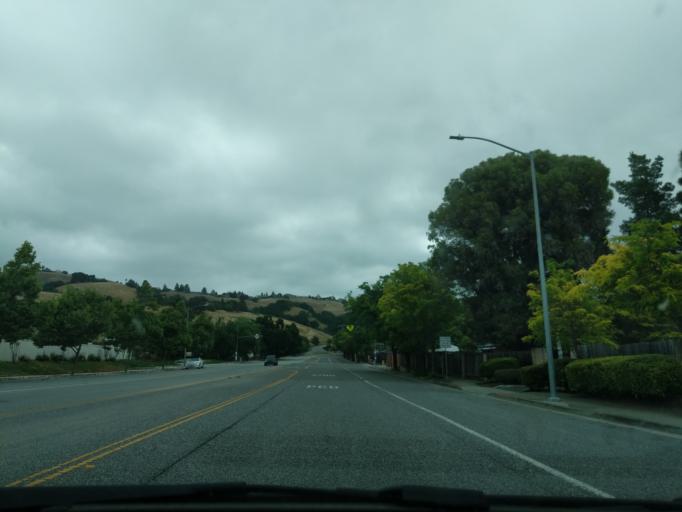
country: US
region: California
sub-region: Santa Clara County
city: Morgan Hill
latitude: 37.1403
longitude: -121.6106
